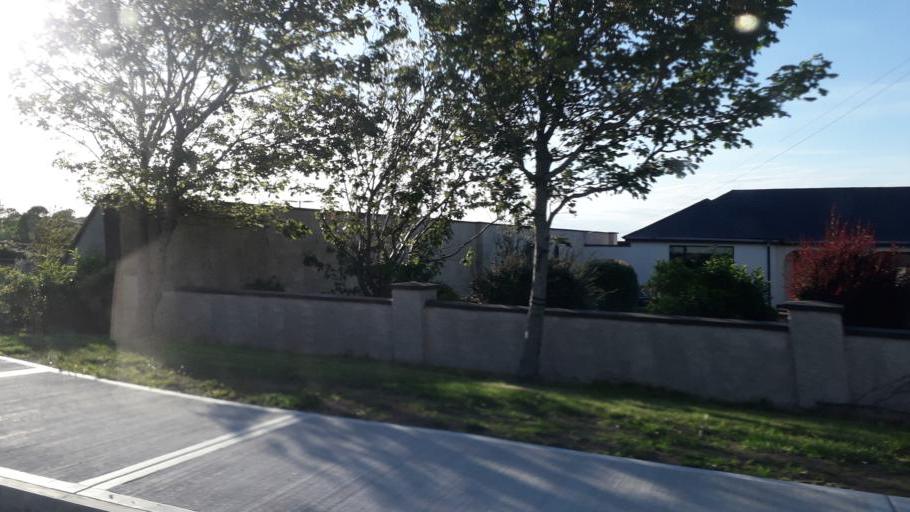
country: IE
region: Leinster
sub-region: Loch Garman
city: Loch Garman
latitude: 52.3413
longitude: -6.4909
